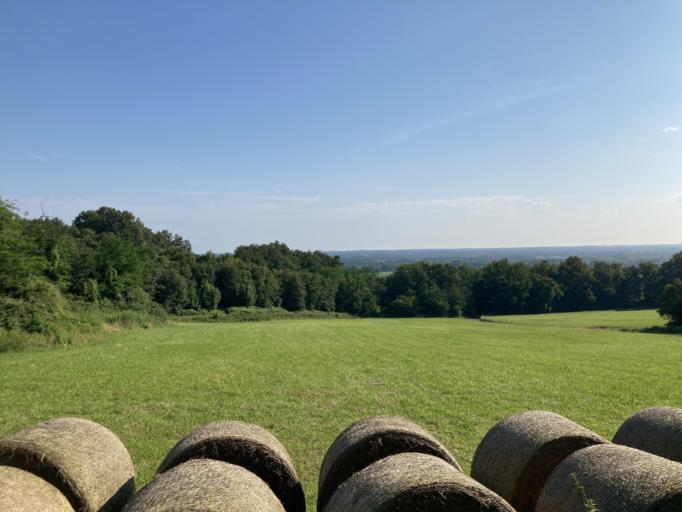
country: FR
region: Aquitaine
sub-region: Departement des Landes
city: Mugron
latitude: 43.7471
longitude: -0.7133
